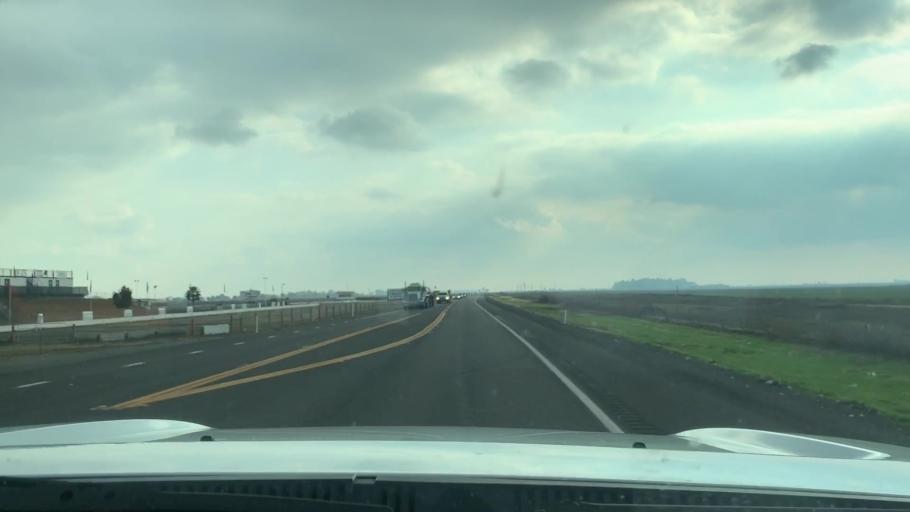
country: US
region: California
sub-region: Kings County
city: Lemoore
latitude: 36.2689
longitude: -119.8078
